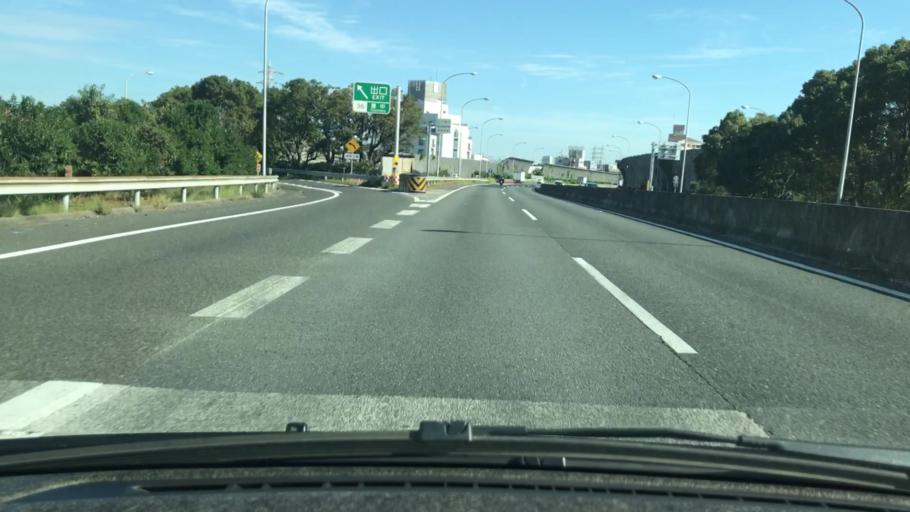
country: JP
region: Osaka
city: Toyonaka
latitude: 34.7536
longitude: 135.4648
